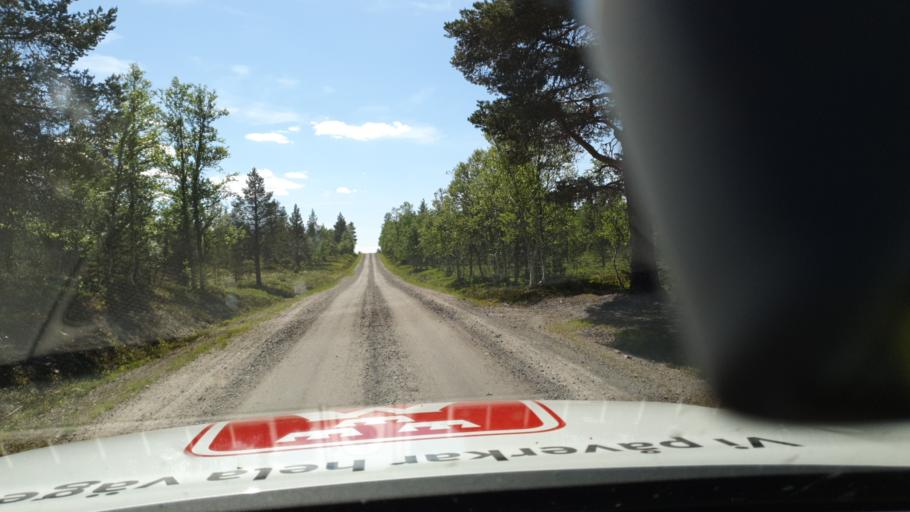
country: NO
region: Hedmark
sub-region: Engerdal
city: Engerdal
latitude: 62.1407
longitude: 12.9424
